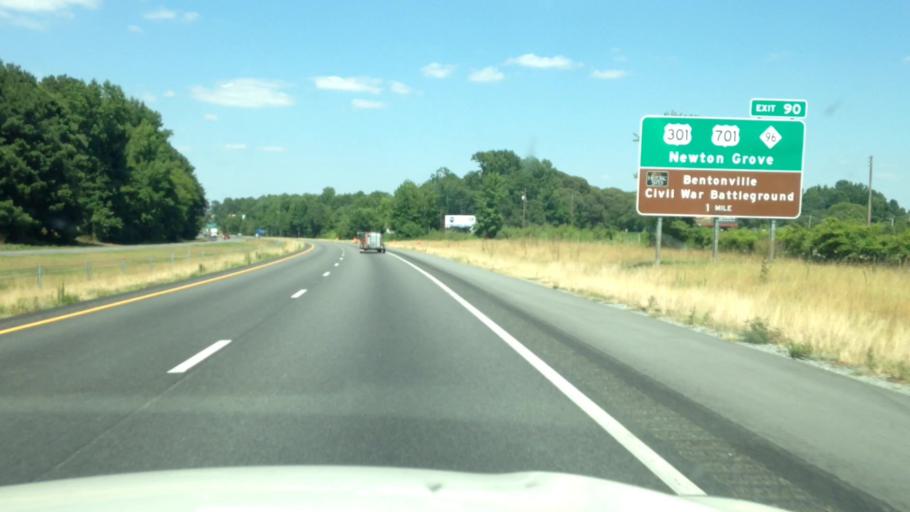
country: US
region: North Carolina
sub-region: Johnston County
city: Four Oaks
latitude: 35.4452
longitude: -78.4036
